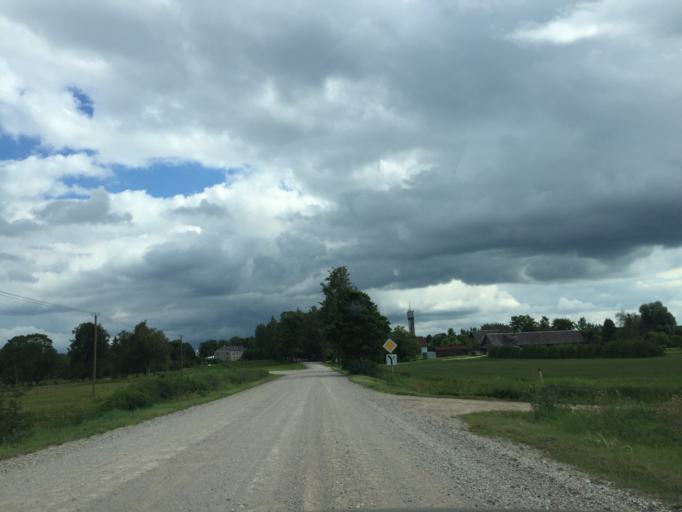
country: LV
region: Malpils
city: Malpils
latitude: 56.8623
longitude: 25.0162
